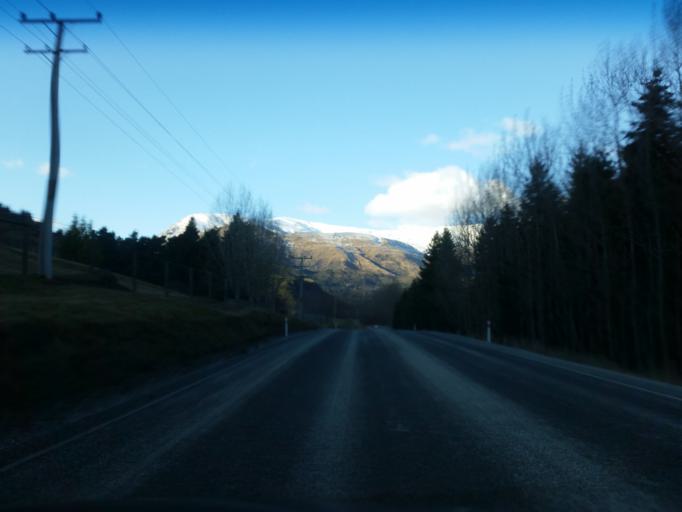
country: NZ
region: Otago
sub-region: Queenstown-Lakes District
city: Arrowtown
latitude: -44.9456
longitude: 168.7986
